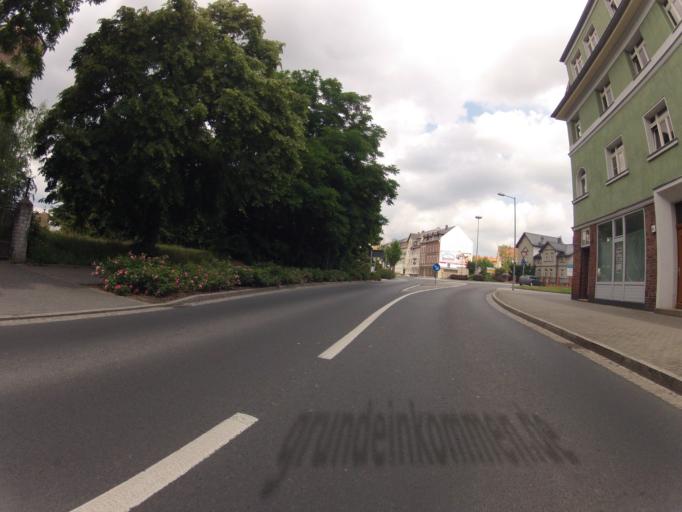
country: DE
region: Saxony
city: Wurzen
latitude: 51.3694
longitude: 12.7449
